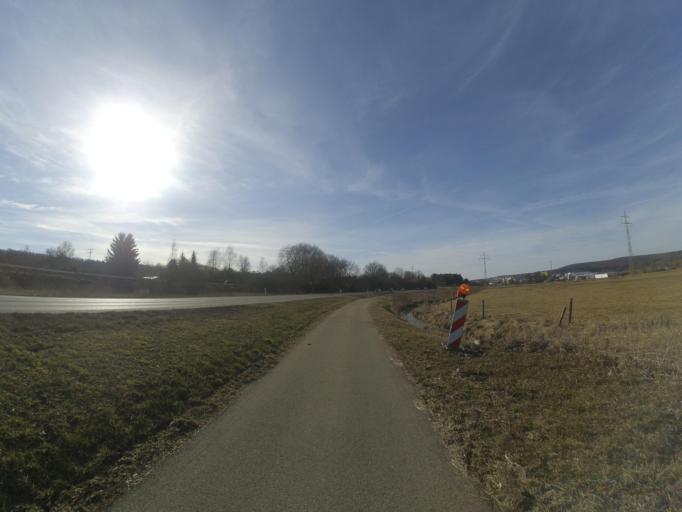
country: DE
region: Baden-Wuerttemberg
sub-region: Regierungsbezirk Stuttgart
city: Giengen an der Brenz
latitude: 48.6238
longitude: 10.2132
